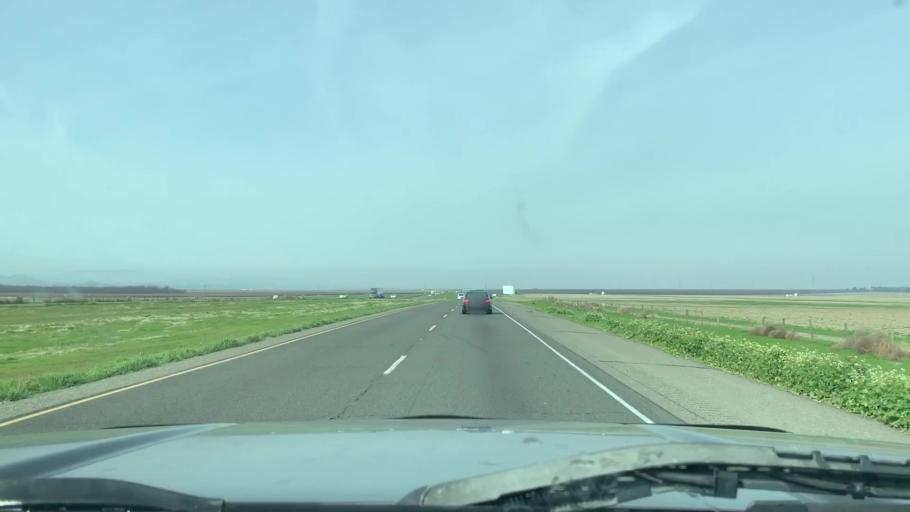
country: US
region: California
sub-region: Fresno County
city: Coalinga
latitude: 36.3467
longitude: -120.3143
